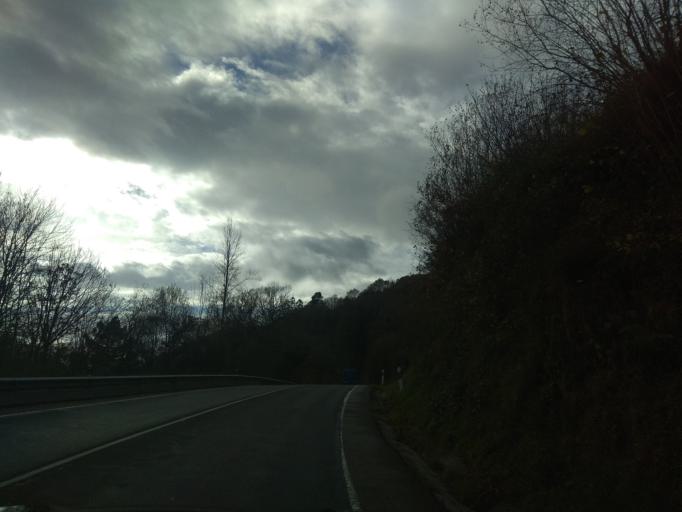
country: ES
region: Cantabria
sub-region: Provincia de Cantabria
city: San Pedro del Romeral
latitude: 43.1578
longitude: -3.8959
